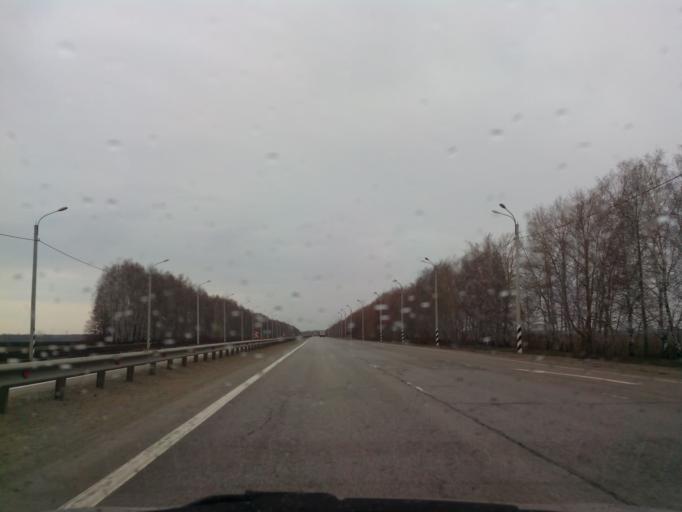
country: RU
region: Tambov
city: Selezni
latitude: 52.7605
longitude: 41.1329
